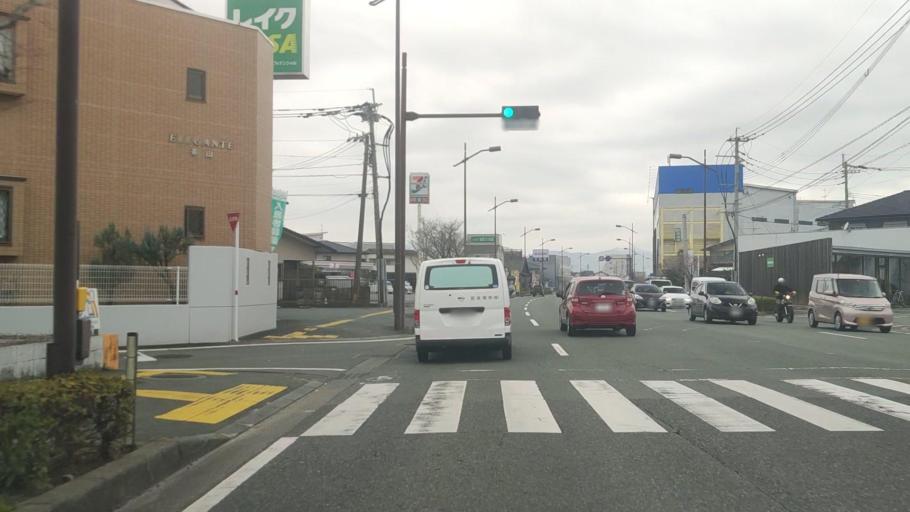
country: JP
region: Kumamoto
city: Kumamoto
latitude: 32.8047
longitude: 130.7571
